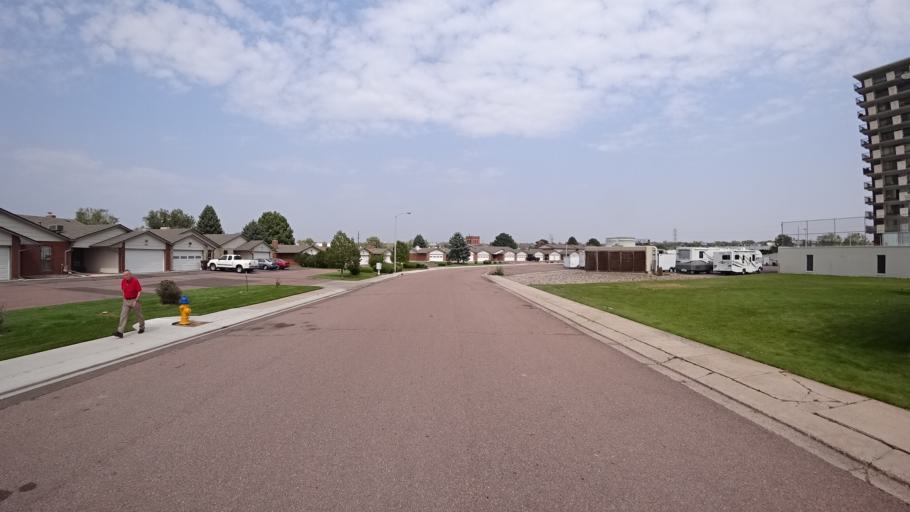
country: US
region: Colorado
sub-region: El Paso County
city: Stratmoor
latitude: 38.8233
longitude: -104.7605
